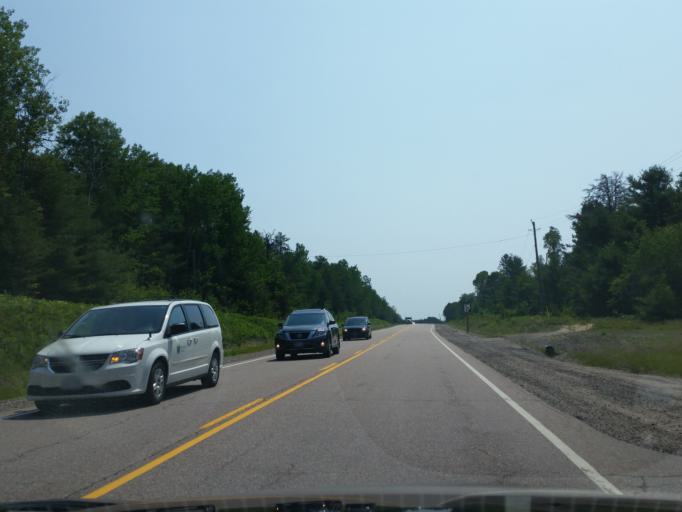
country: CA
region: Ontario
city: Deep River
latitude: 46.1861
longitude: -77.8630
